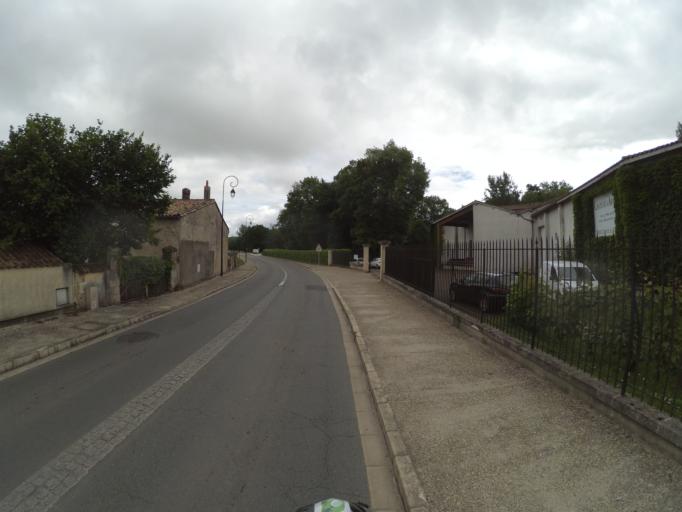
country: FR
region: Aquitaine
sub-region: Departement de la Gironde
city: Lamarque
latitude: 45.0709
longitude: -0.7240
